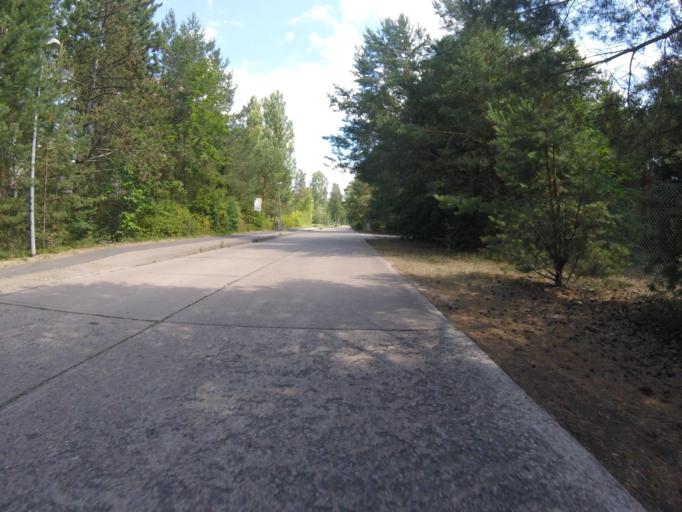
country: DE
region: Berlin
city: Schmockwitz
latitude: 52.3422
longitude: 13.6656
